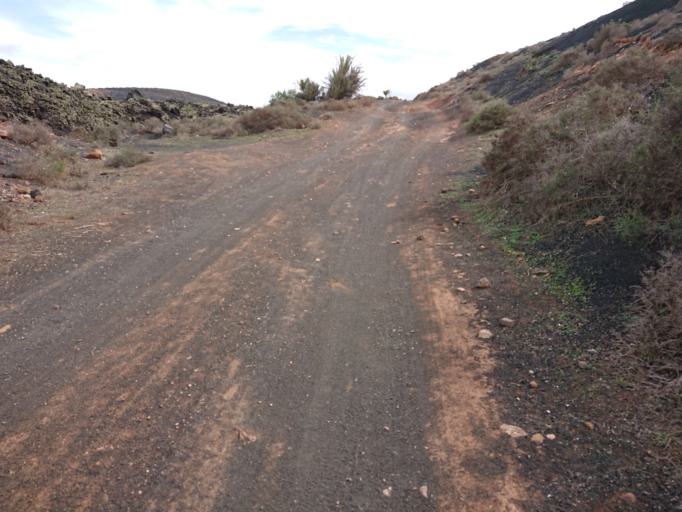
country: ES
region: Canary Islands
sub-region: Provincia de Las Palmas
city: Tinajo
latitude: 29.0199
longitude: -13.6766
